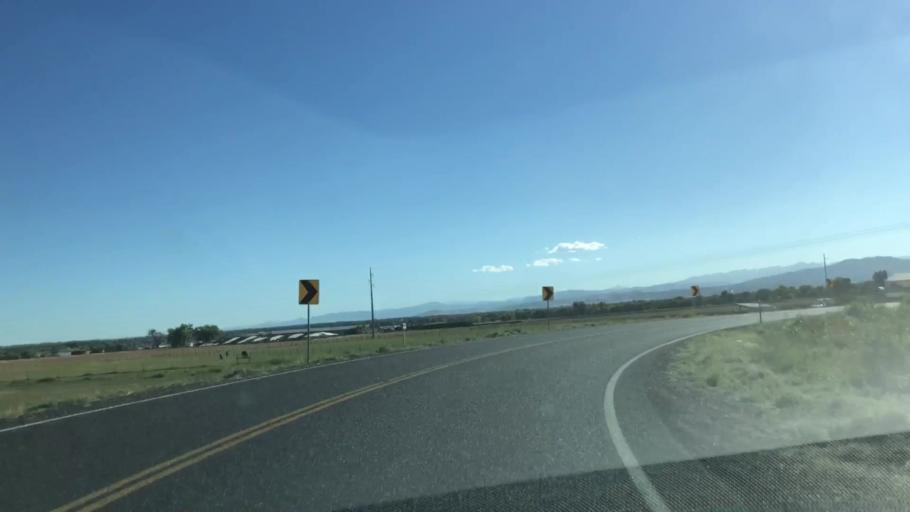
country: US
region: Colorado
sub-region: Larimer County
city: Loveland
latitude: 40.4608
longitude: -105.0495
